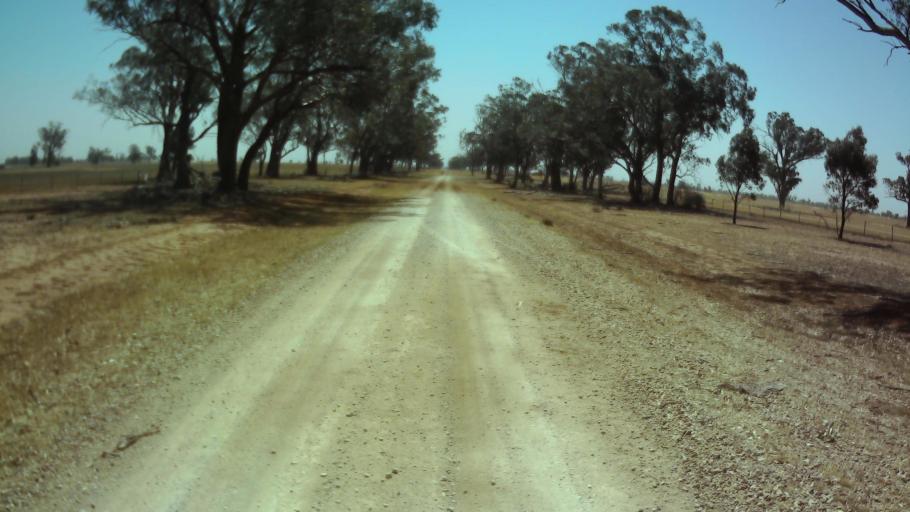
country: AU
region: New South Wales
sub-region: Weddin
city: Grenfell
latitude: -34.0127
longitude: 147.8948
